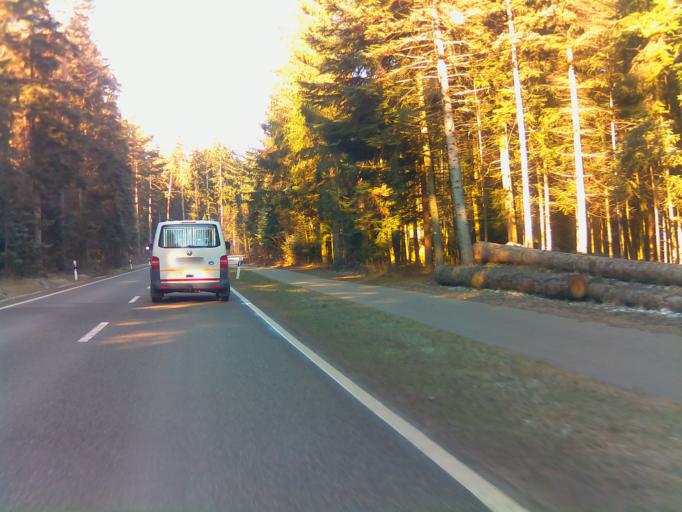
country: DE
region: Baden-Wuerttemberg
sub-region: Karlsruhe Region
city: Oberreichenbach
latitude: 48.7269
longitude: 8.6601
